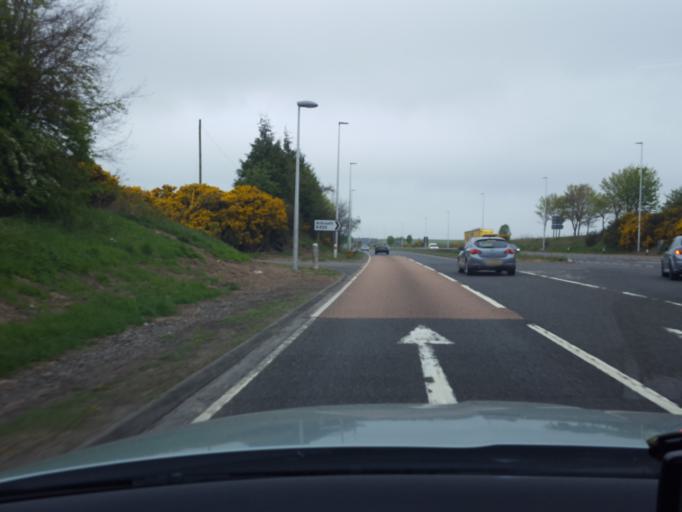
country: GB
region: Scotland
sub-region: Angus
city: Forfar
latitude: 56.6179
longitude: -2.9034
